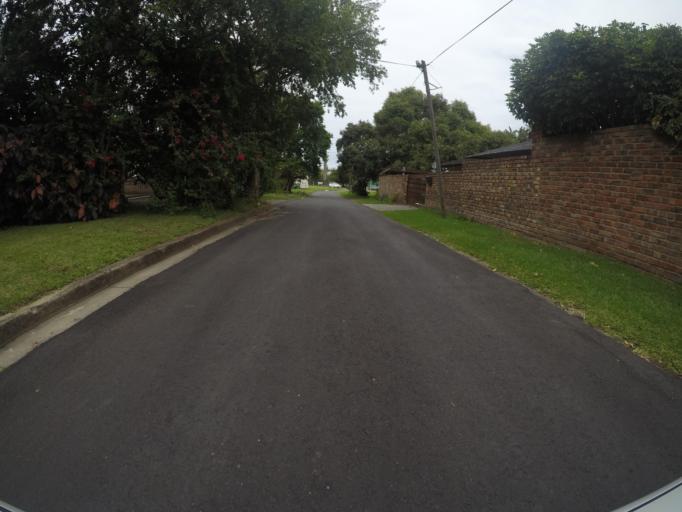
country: ZA
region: Eastern Cape
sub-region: Buffalo City Metropolitan Municipality
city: East London
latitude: -32.9727
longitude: 27.9315
